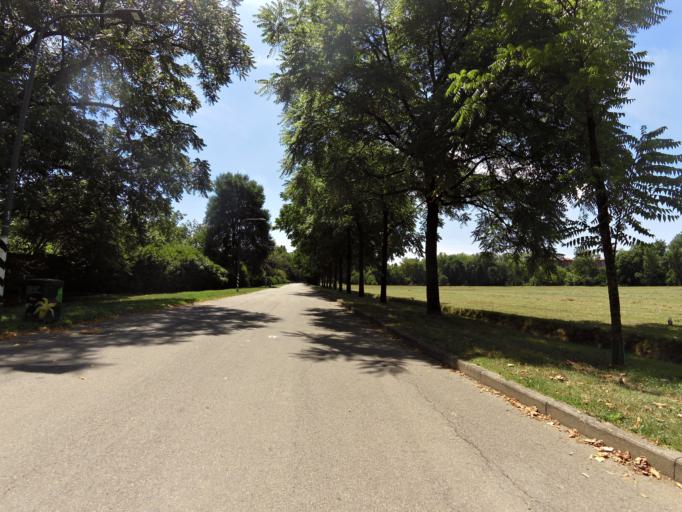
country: IT
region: Lombardy
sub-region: Citta metropolitana di Milano
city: Novegro-Tregarezzo-San Felice
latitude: 45.4946
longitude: 9.2520
